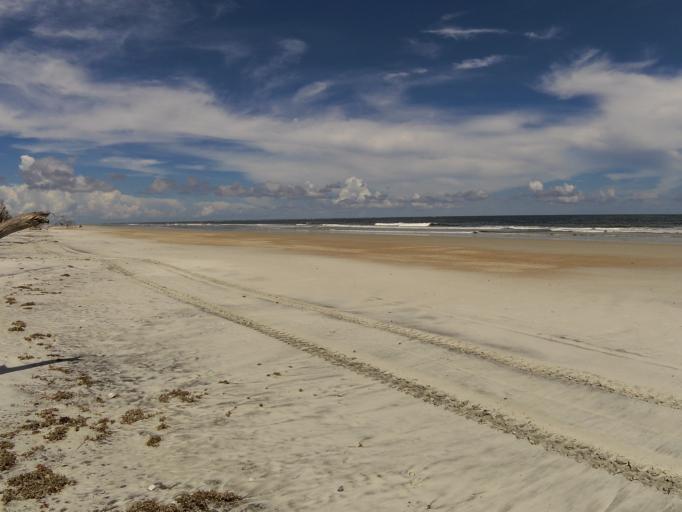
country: US
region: Florida
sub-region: Duval County
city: Atlantic Beach
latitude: 30.4729
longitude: -81.4131
